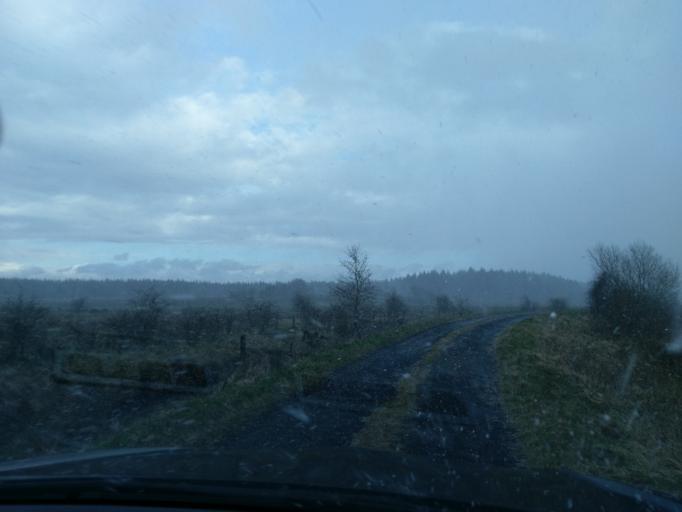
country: IE
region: Connaught
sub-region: County Galway
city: Athenry
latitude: 53.4060
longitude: -8.5966
